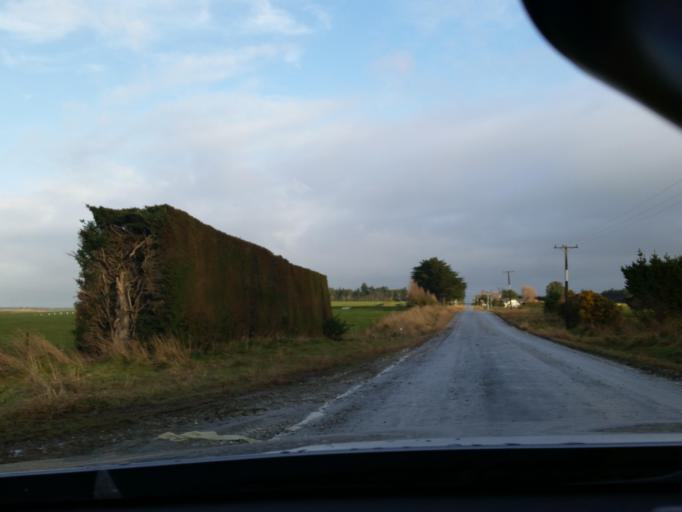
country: NZ
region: Southland
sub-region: Invercargill City
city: Invercargill
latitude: -46.4113
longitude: 168.5061
